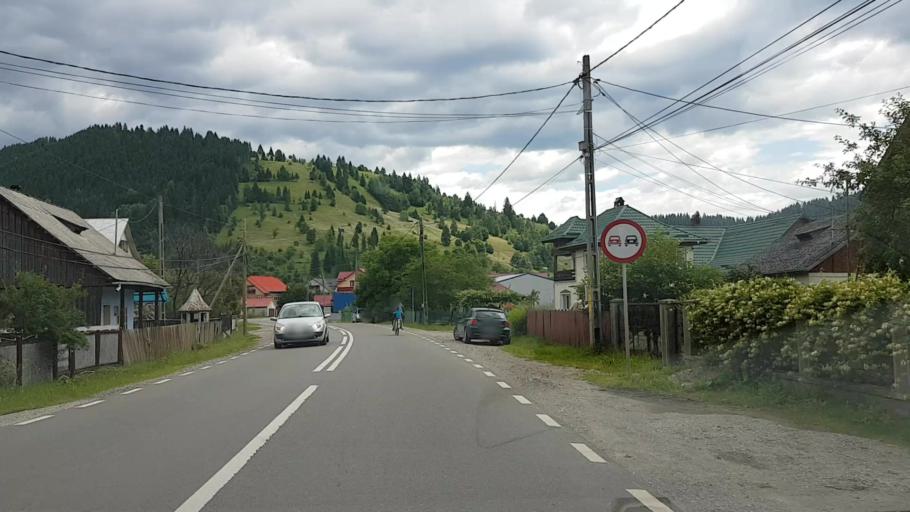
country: RO
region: Neamt
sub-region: Comuna Farcasa
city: Farcasa
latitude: 47.1575
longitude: 25.8341
